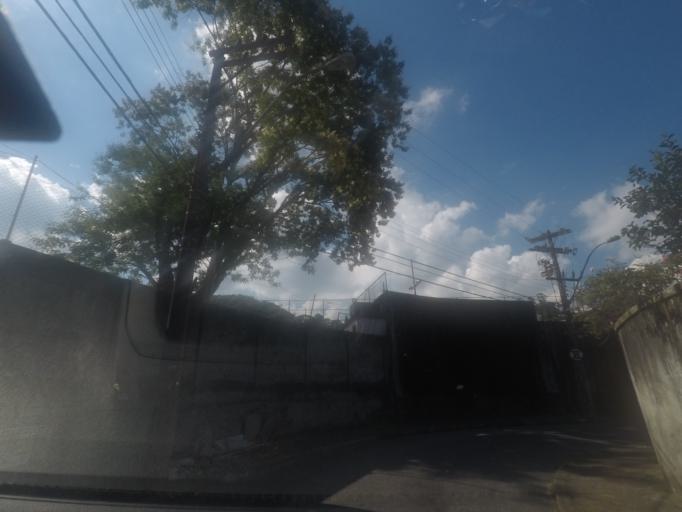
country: BR
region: Rio de Janeiro
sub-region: Petropolis
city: Petropolis
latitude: -22.5198
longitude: -43.1923
